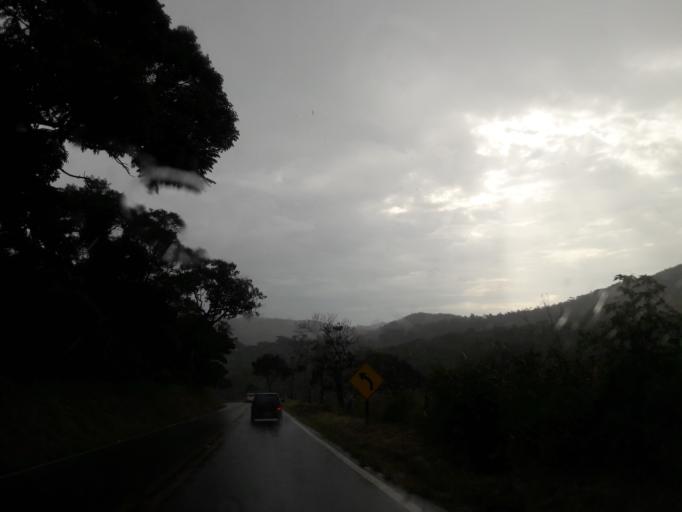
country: BR
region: Sao Paulo
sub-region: Aruja
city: Aruja
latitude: -23.3014
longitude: -46.4342
